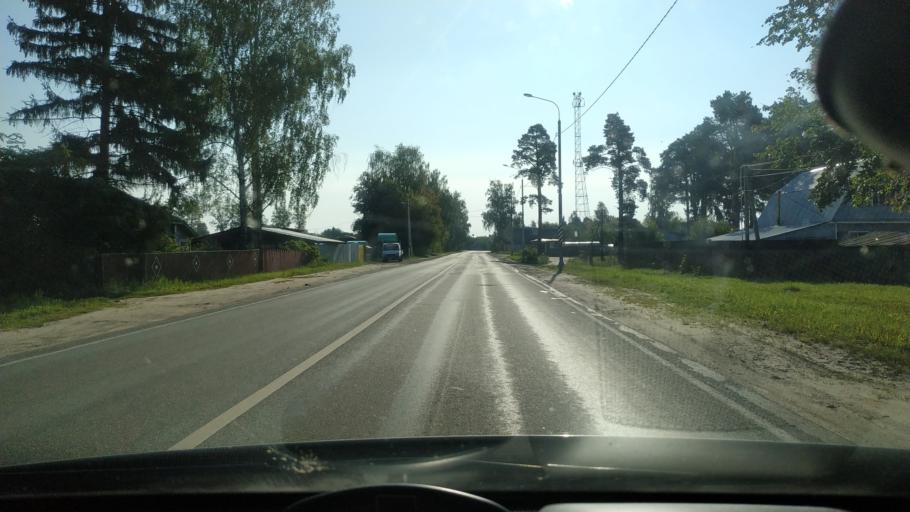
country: RU
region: Moskovskaya
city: Kerva
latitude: 55.5620
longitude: 39.6702
